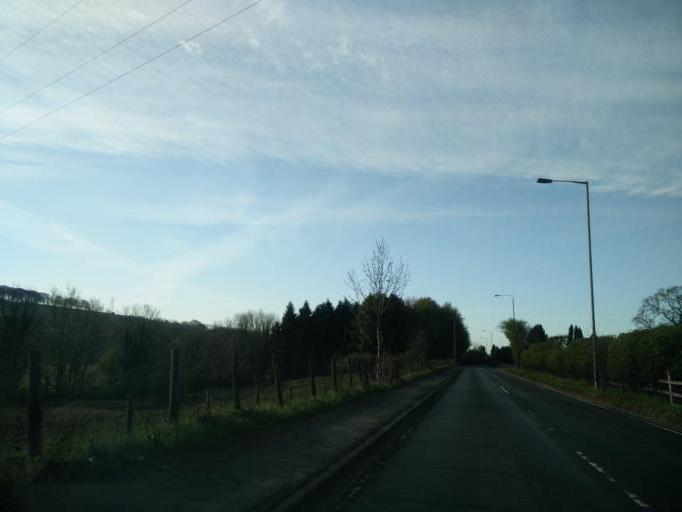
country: GB
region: England
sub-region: County Durham
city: Crook
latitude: 54.6998
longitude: -1.7497
